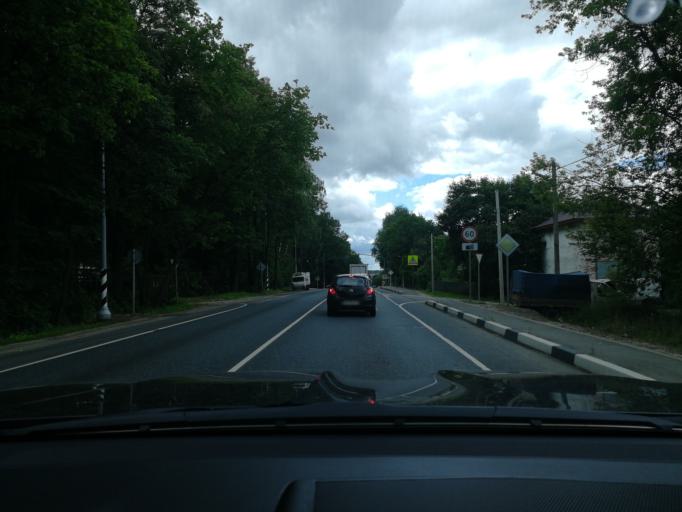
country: RU
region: Moskovskaya
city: Popovo
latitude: 55.0616
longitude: 37.7738
